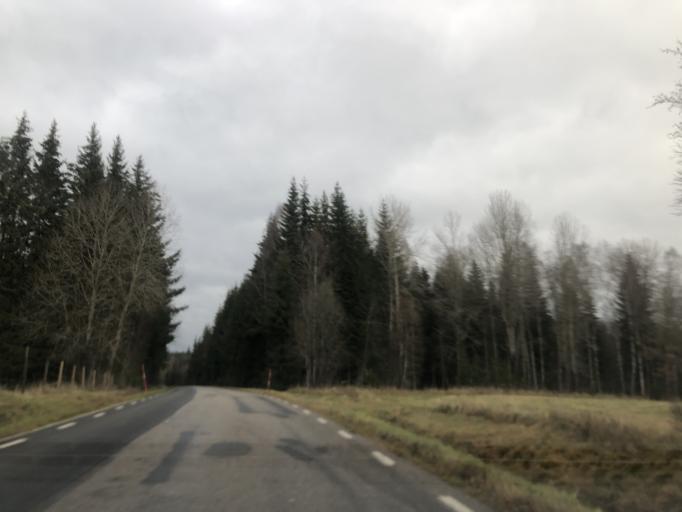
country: SE
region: Vaestra Goetaland
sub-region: Boras Kommun
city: Dalsjofors
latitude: 57.8181
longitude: 13.1968
